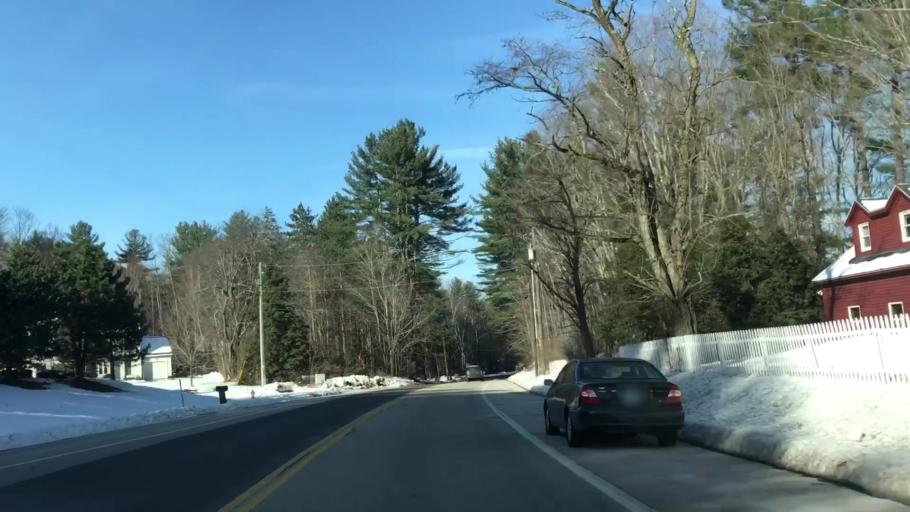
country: US
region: New Hampshire
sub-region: Hillsborough County
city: Milford
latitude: 42.8461
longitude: -71.6158
